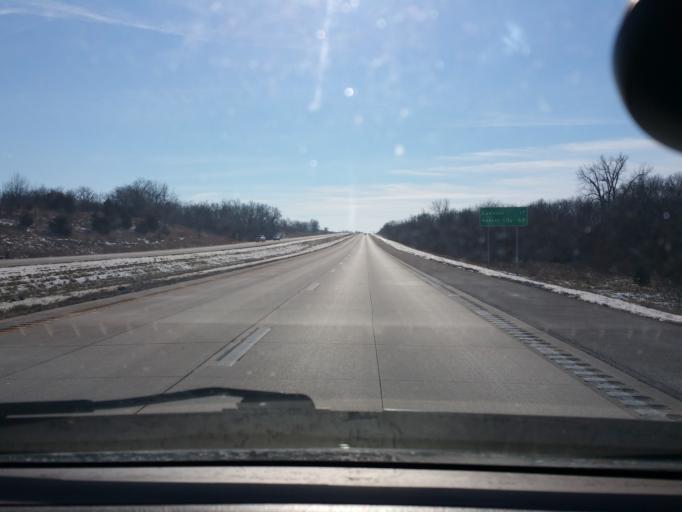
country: US
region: Missouri
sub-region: Daviess County
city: Gallatin
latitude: 39.9851
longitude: -94.0950
